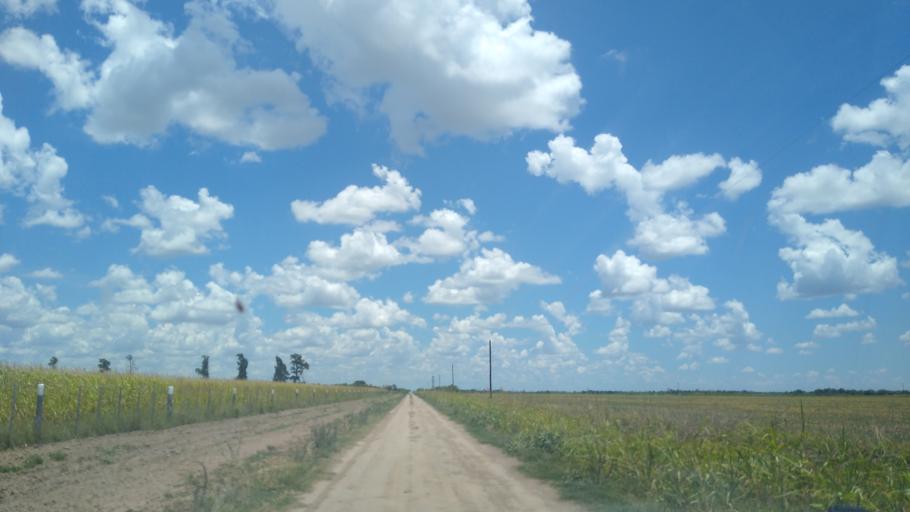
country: AR
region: Chaco
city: Presidencia Roque Saenz Pena
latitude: -26.7428
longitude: -60.3522
